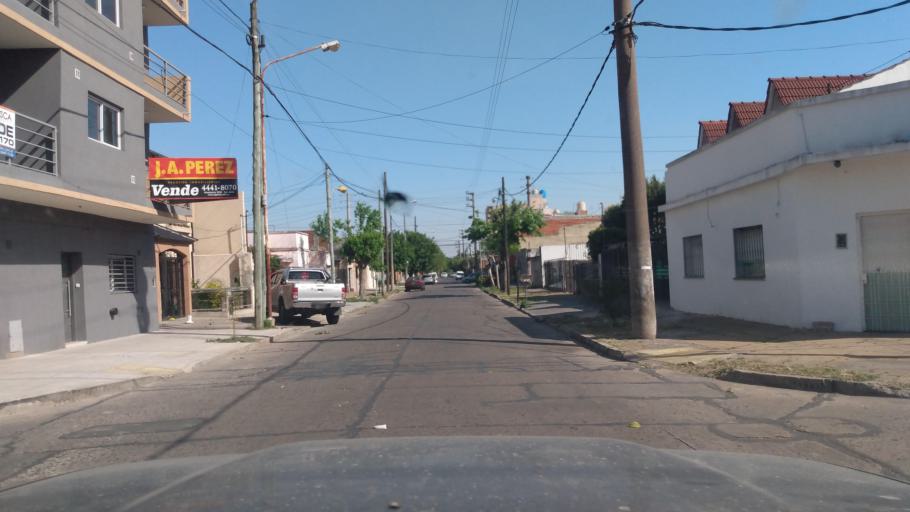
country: AR
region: Buenos Aires
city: San Justo
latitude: -34.6713
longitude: -58.5753
